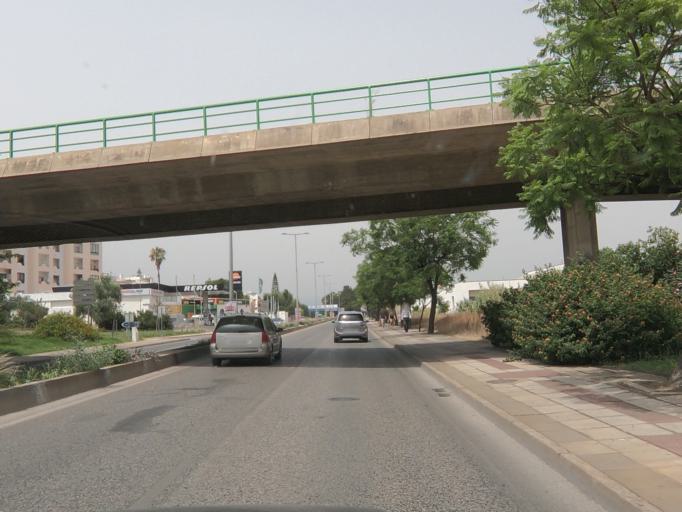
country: PT
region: Faro
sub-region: Portimao
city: Portimao
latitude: 37.1367
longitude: -8.5458
